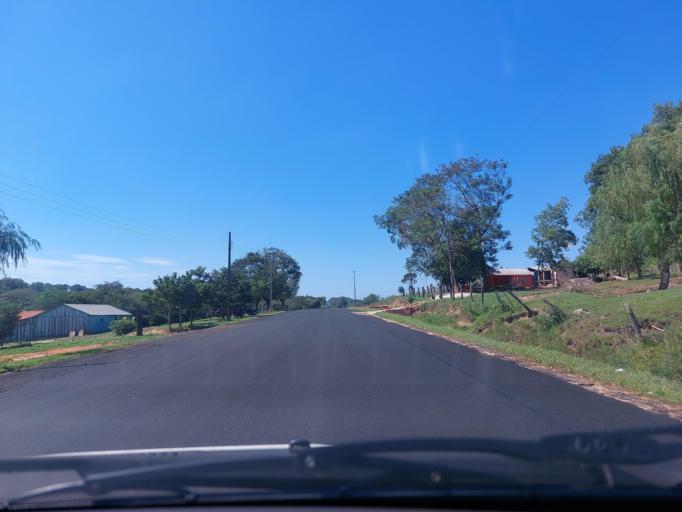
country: PY
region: San Pedro
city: Guayaybi
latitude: -24.5501
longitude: -56.5165
